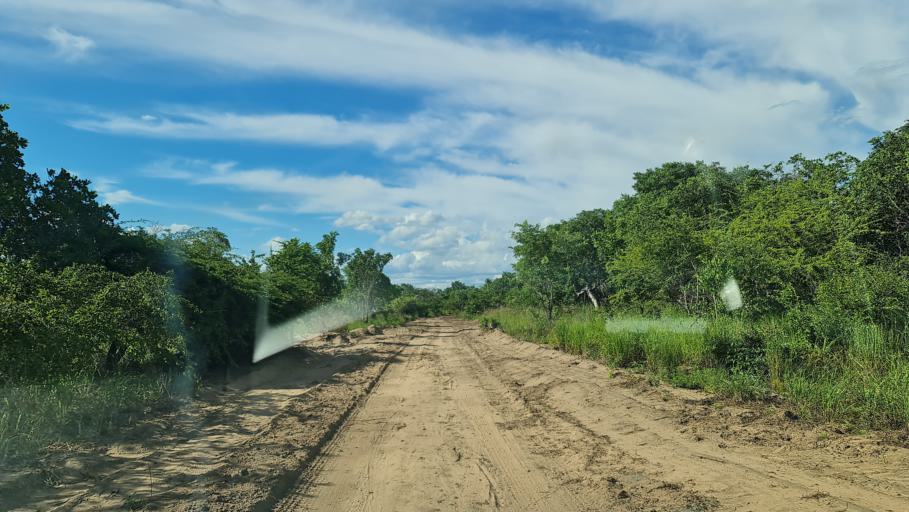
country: MZ
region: Nampula
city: Antonio Enes
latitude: -15.5269
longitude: 40.1269
